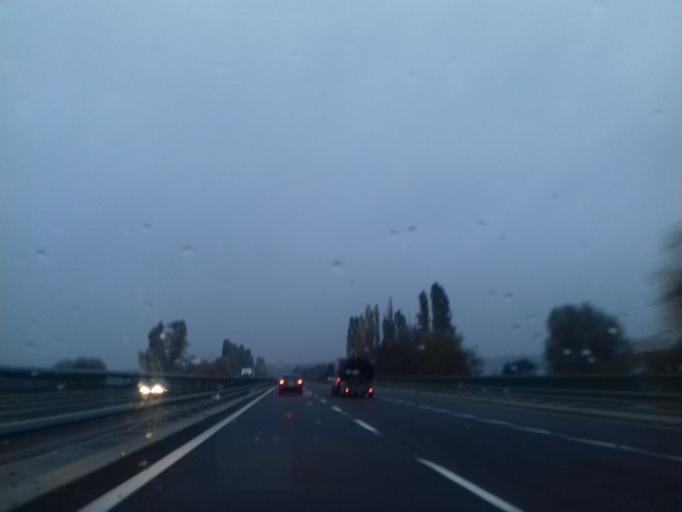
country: CZ
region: Olomoucky
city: Litovel
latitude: 49.6908
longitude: 17.0494
